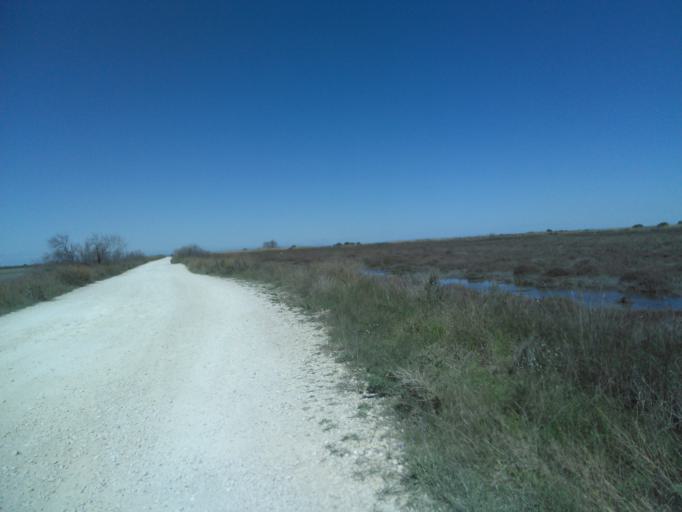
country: FR
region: Provence-Alpes-Cote d'Azur
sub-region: Departement des Bouches-du-Rhone
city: Saintes-Maries-de-la-Mer
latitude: 43.4517
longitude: 4.5907
